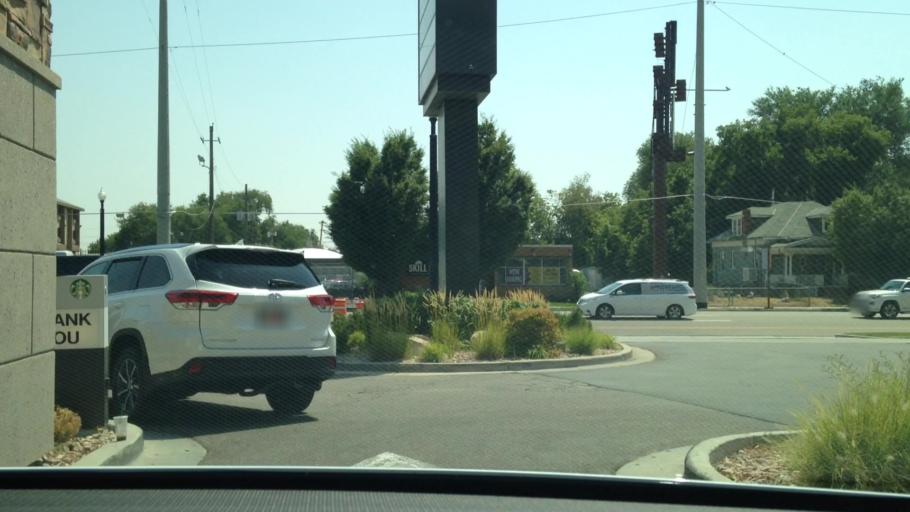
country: US
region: Utah
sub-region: Salt Lake County
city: Salt Lake City
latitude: 40.7567
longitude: -111.8978
